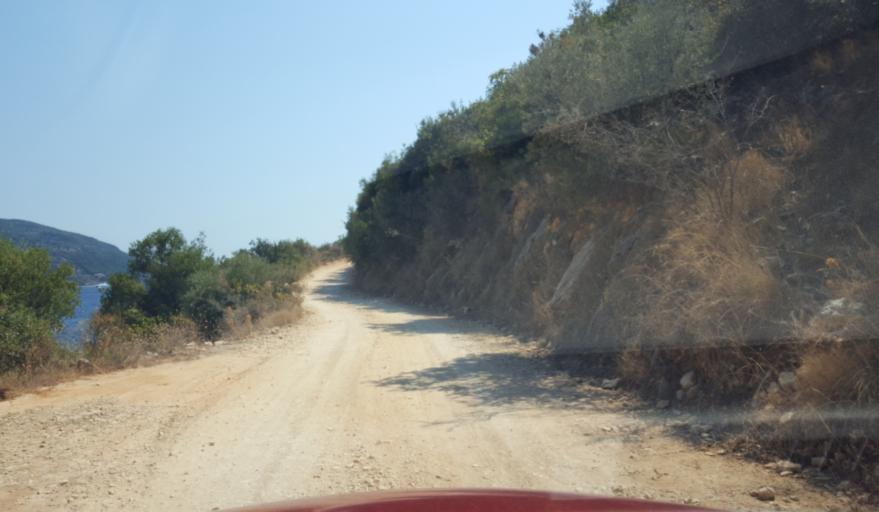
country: GR
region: Ionian Islands
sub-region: Lefkada
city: Nidri
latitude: 38.6600
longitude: 20.7169
